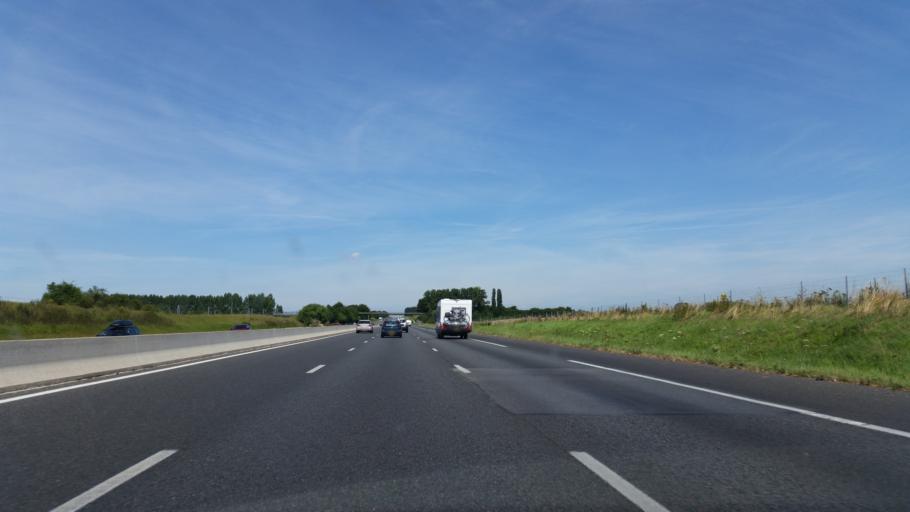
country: FR
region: Nord-Pas-de-Calais
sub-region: Departement du Pas-de-Calais
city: Vaulx-Vraucourt
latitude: 50.1430
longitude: 2.8725
